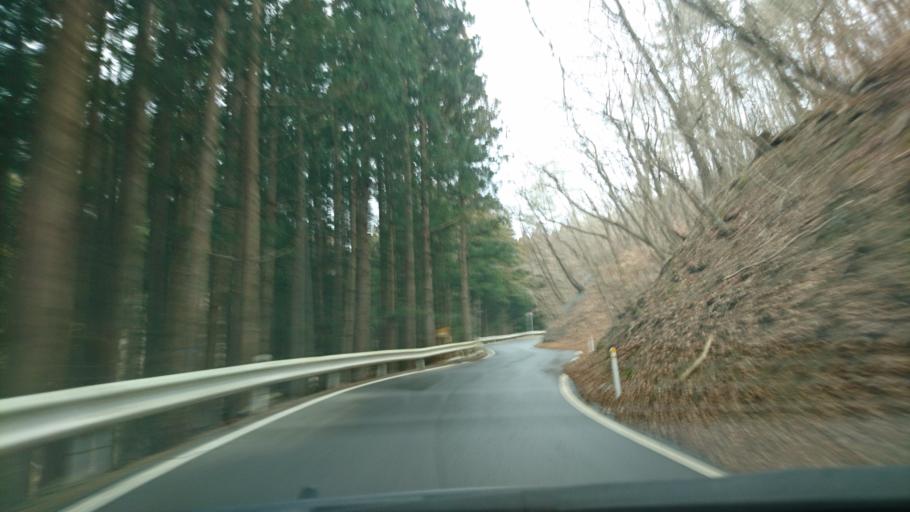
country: JP
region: Iwate
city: Ofunato
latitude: 38.9932
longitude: 141.5481
